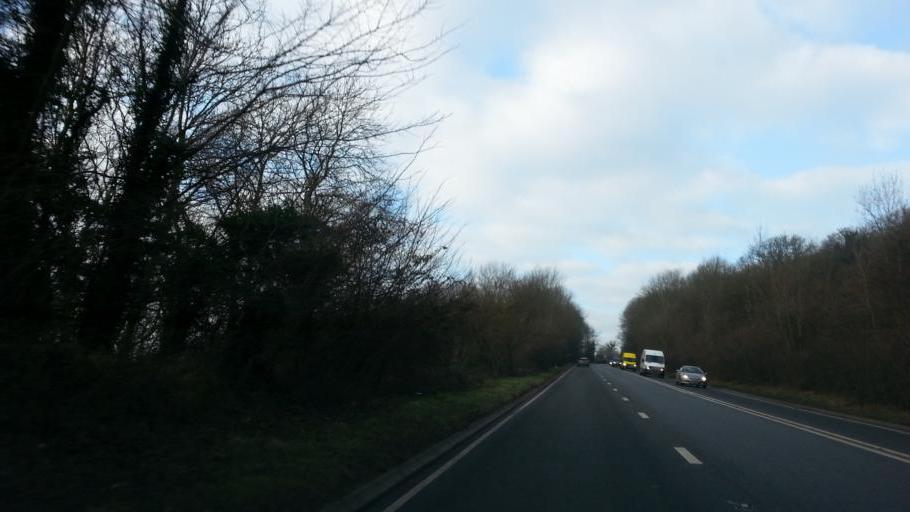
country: GB
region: England
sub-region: South Gloucestershire
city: Cold Ashton
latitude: 51.4186
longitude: -2.3515
